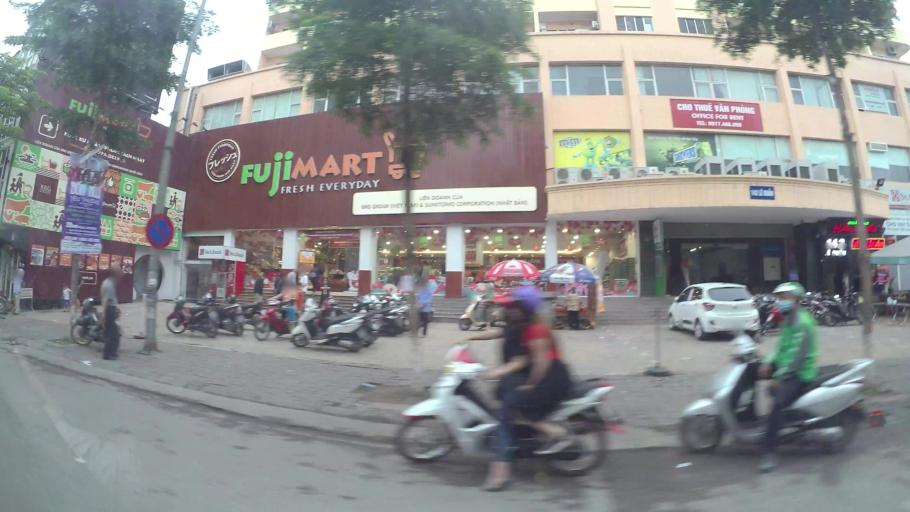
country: VN
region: Ha Noi
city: Hanoi
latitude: 21.0185
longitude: 105.8413
